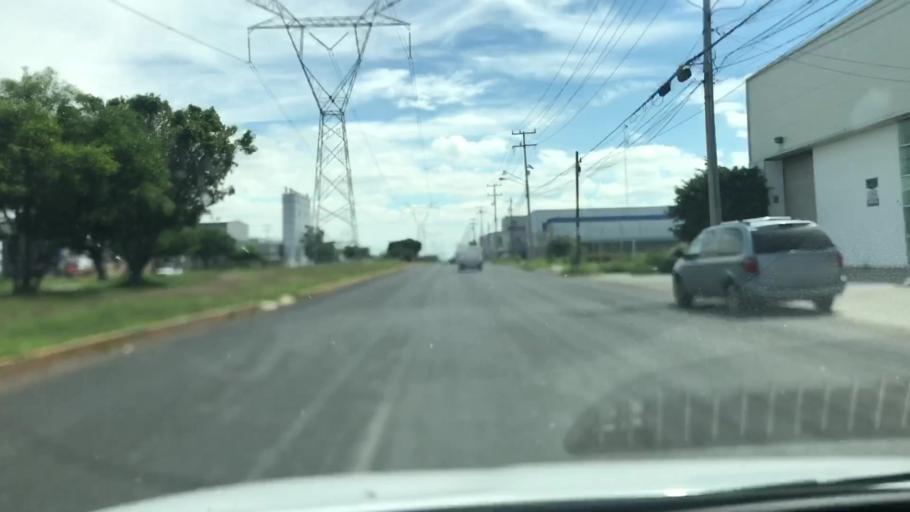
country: MX
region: Guanajuato
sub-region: Celaya
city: La Trinidad
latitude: 20.5501
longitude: -100.7992
